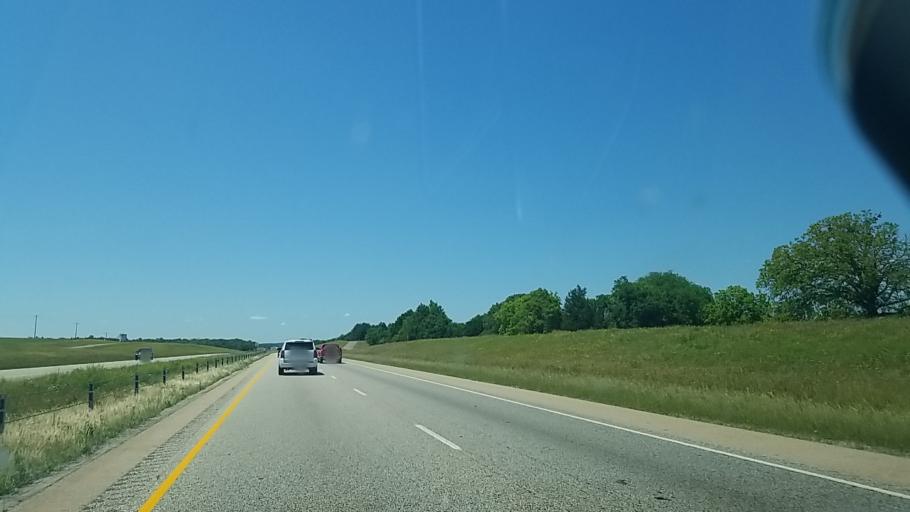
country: US
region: Texas
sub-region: Leon County
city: Buffalo
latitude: 31.3878
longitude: -96.0268
